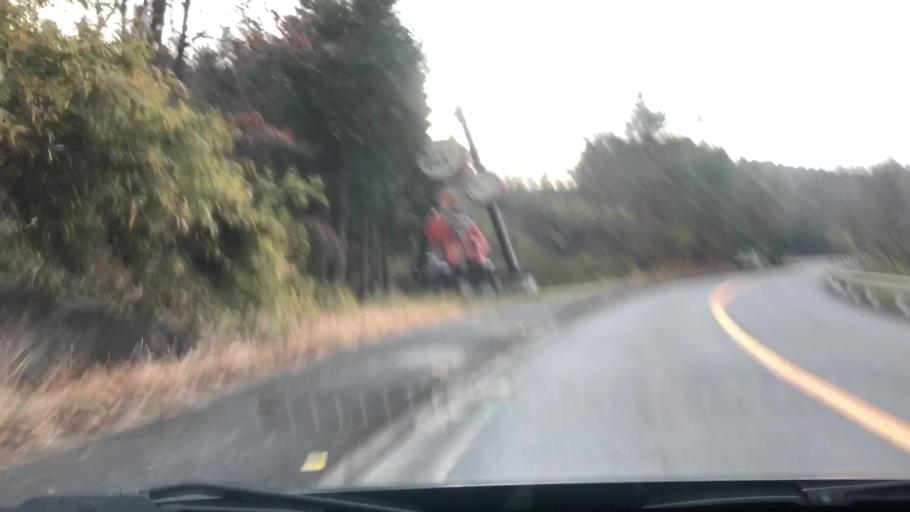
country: JP
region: Oita
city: Takedamachi
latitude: 32.9708
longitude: 131.5049
